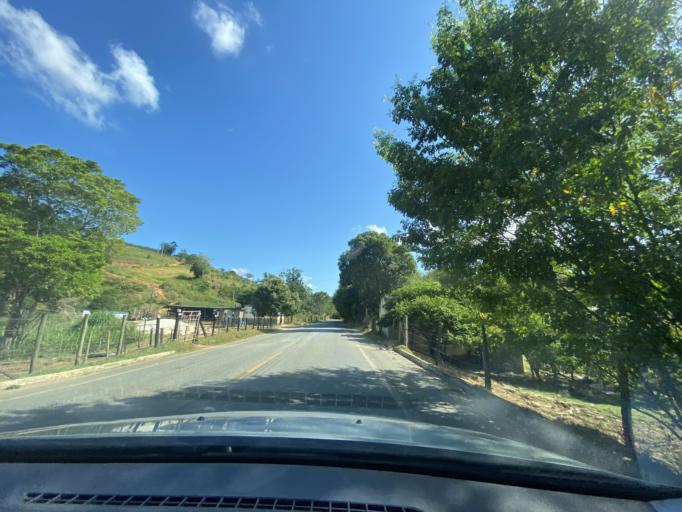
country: BR
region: Espirito Santo
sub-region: Jeronimo Monteiro
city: Jeronimo Monteiro
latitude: -20.7866
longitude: -41.4115
